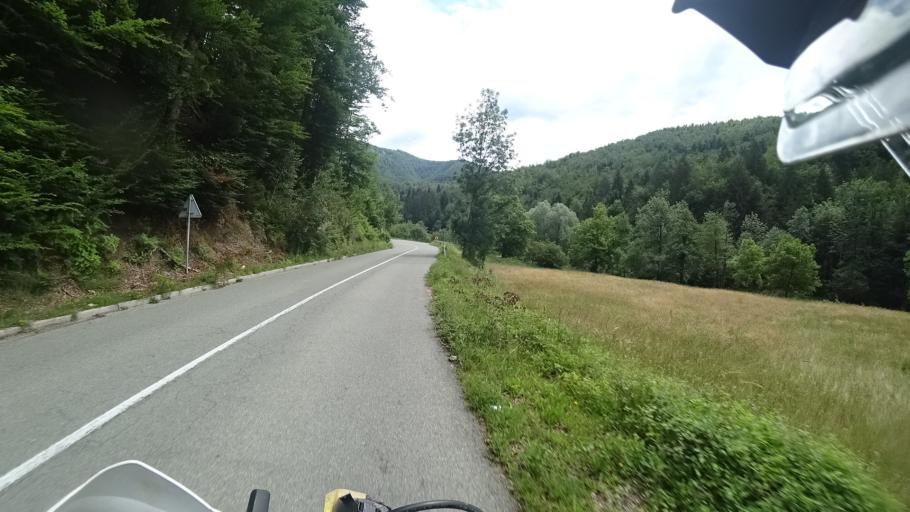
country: SI
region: Osilnica
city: Osilnica
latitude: 45.5566
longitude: 14.6916
